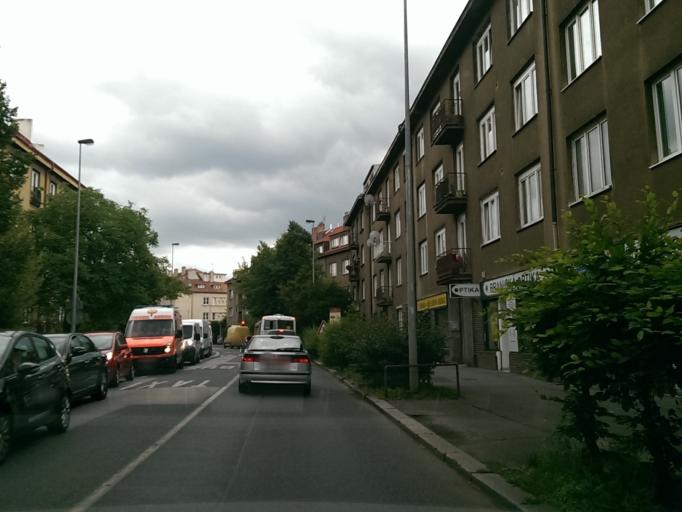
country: CZ
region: Praha
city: Branik
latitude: 50.0377
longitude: 14.4107
